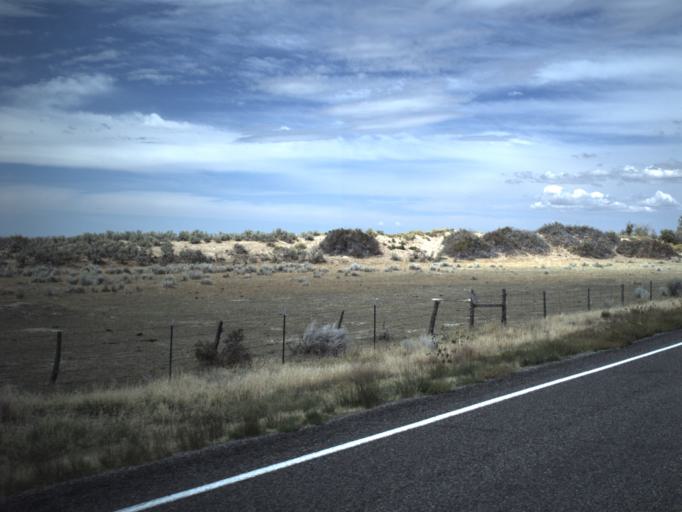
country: US
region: Utah
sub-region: Millard County
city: Fillmore
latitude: 39.1302
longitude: -112.4091
